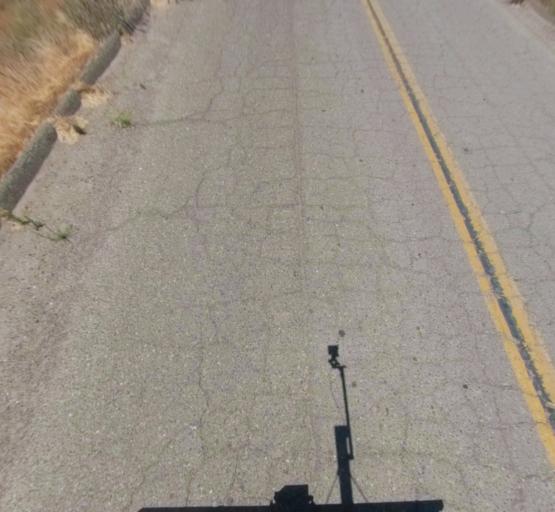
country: US
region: California
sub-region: Merced County
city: Dos Palos
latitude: 37.0546
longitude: -120.4949
